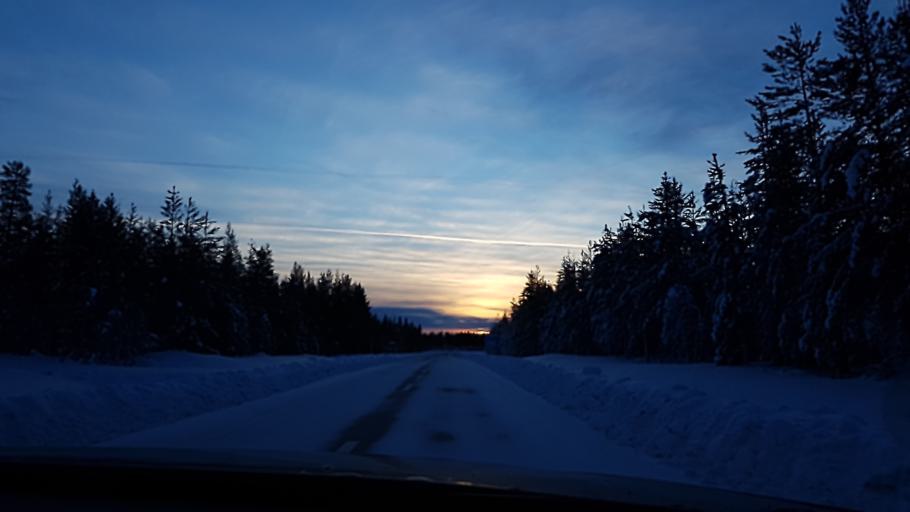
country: SE
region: Norrbotten
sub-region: Jokkmokks Kommun
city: Jokkmokk
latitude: 66.0733
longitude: 20.0749
